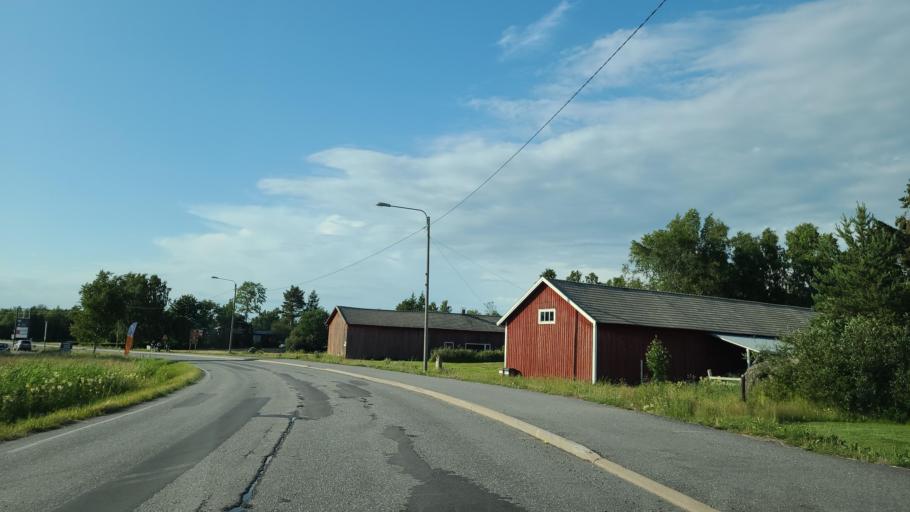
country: FI
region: Ostrobothnia
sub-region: Vaasa
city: Replot
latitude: 63.2302
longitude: 21.4105
